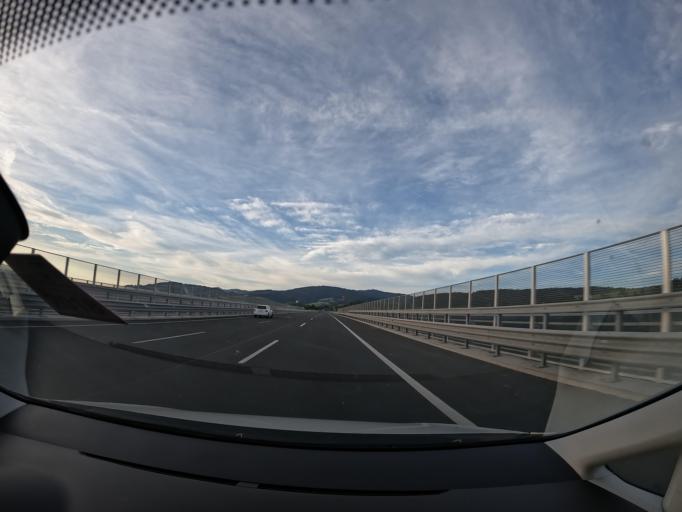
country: AT
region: Carinthia
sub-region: Politischer Bezirk Wolfsberg
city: Bad Sankt Leonhard im Lavanttal
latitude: 46.9287
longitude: 14.8220
